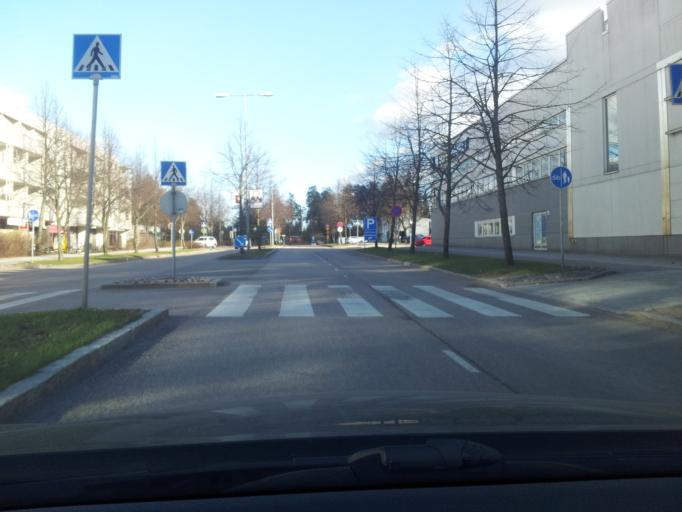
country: FI
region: Uusimaa
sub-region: Helsinki
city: Espoo
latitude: 60.1489
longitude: 24.6574
